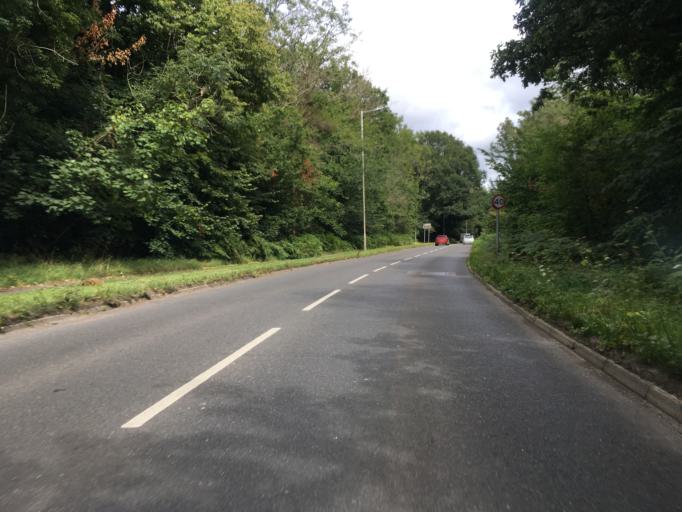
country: GB
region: England
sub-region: Kent
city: Royal Tunbridge Wells
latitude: 51.1317
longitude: 0.2311
